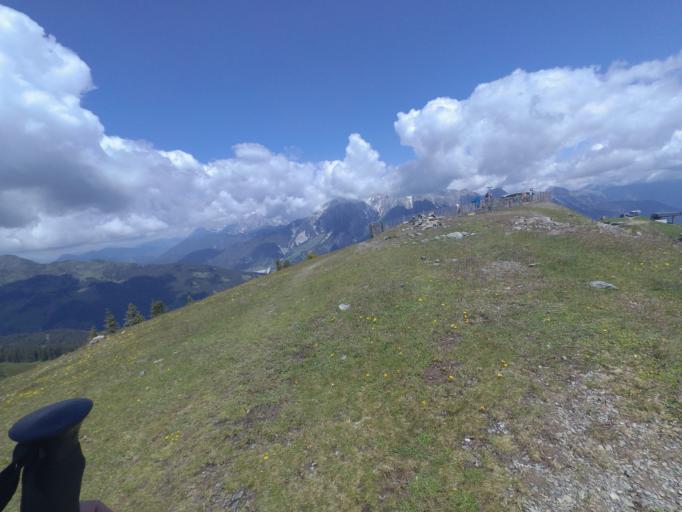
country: AT
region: Salzburg
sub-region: Politischer Bezirk Zell am See
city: Viehhofen
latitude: 47.4020
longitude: 12.7019
